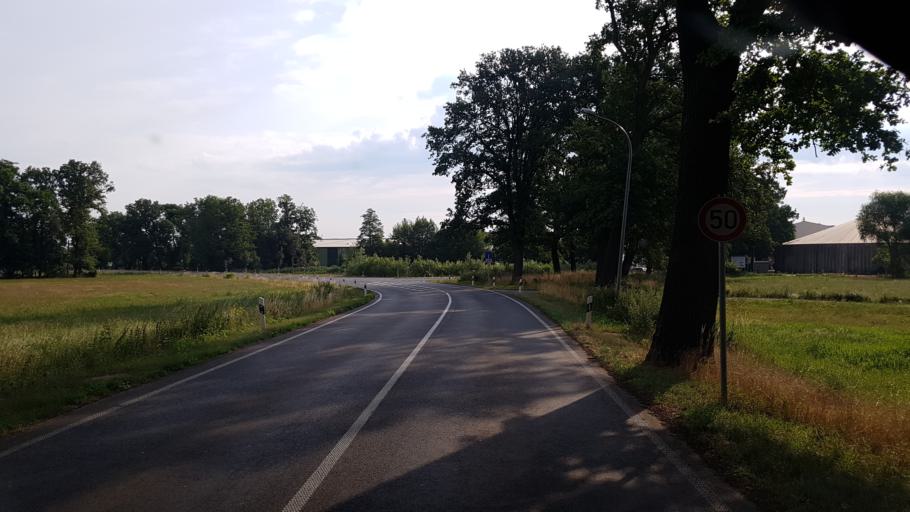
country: DE
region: Brandenburg
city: Golssen
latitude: 51.9713
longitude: 13.5698
